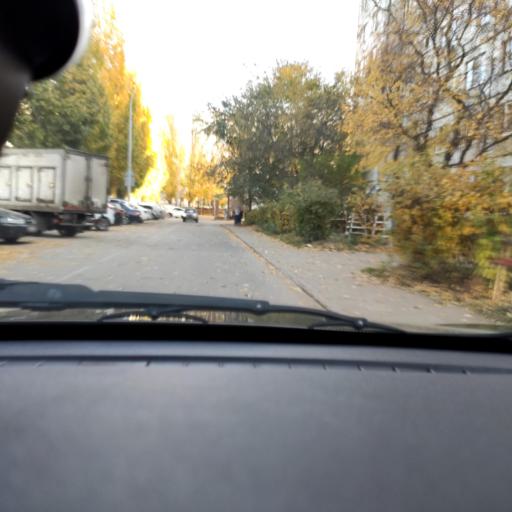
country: RU
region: Samara
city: Tol'yatti
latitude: 53.5209
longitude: 49.3020
